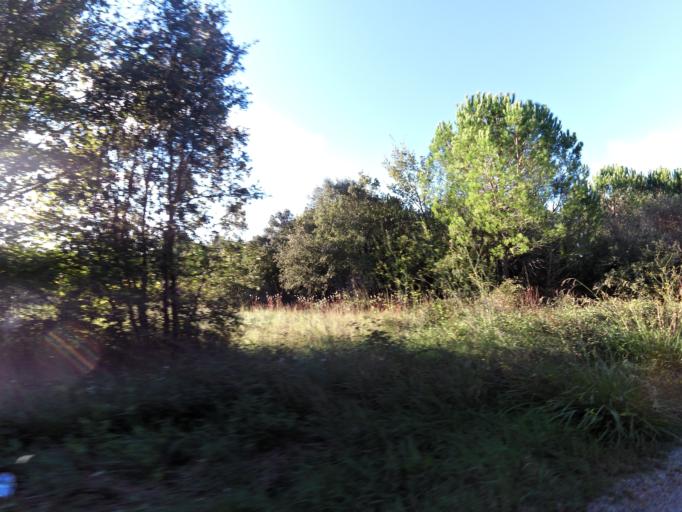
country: FR
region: Languedoc-Roussillon
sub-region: Departement du Gard
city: Villevieille
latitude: 43.7967
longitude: 4.1190
